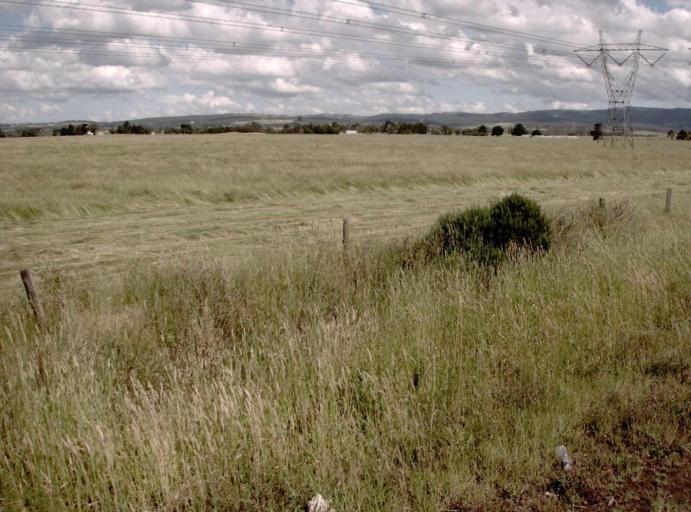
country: AU
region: Victoria
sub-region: Latrobe
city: Morwell
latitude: -38.2599
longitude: 146.4343
